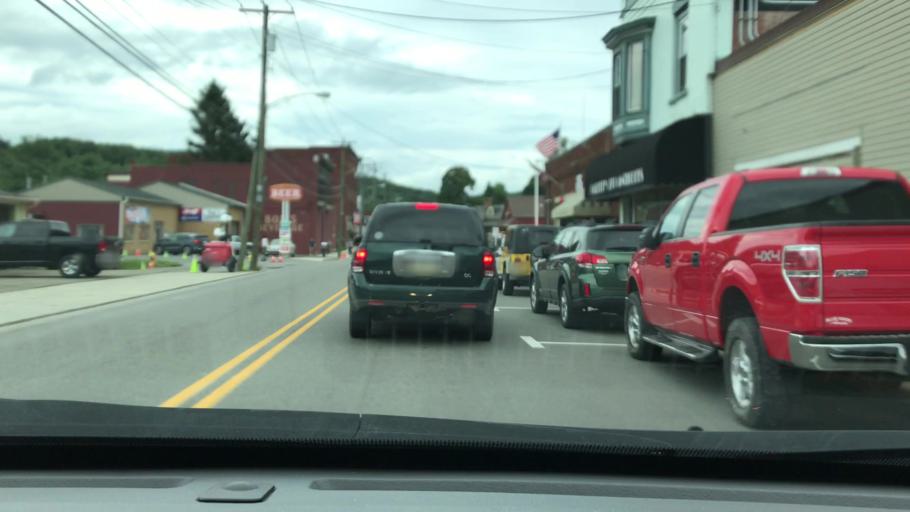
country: US
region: Pennsylvania
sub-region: Elk County
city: Ridgway
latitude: 41.4236
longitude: -78.7305
